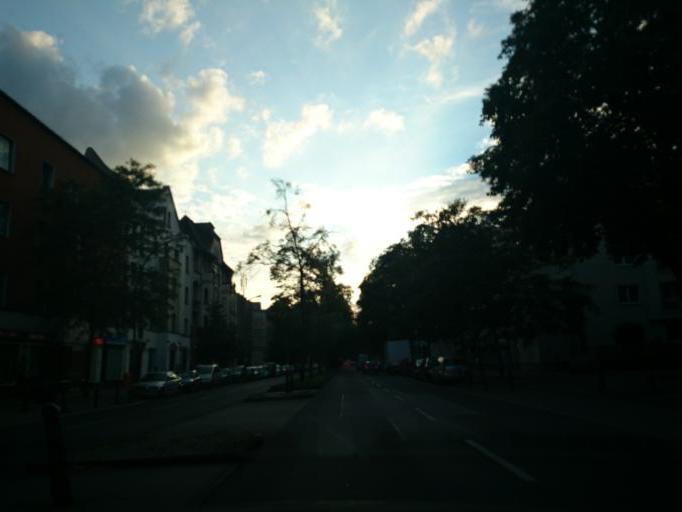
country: DE
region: Berlin
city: Reinickendorf
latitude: 52.5659
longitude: 13.3205
